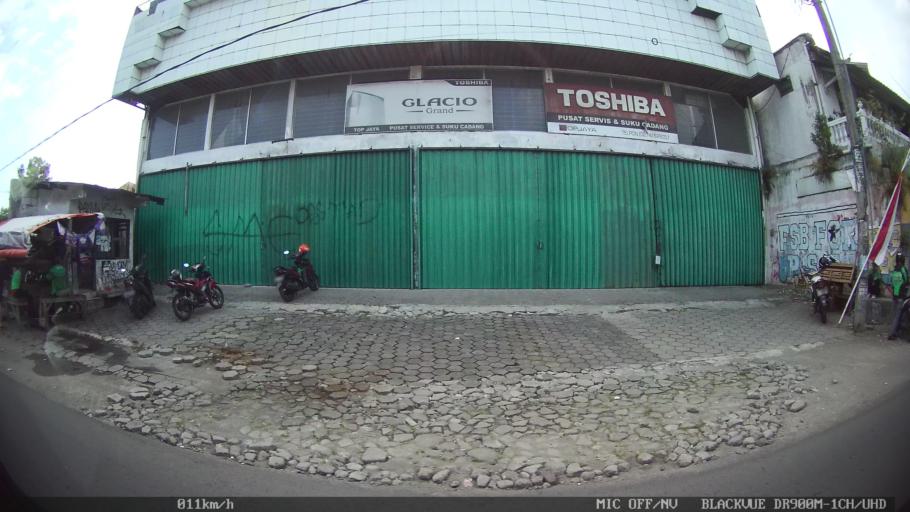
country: ID
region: Daerah Istimewa Yogyakarta
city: Yogyakarta
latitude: -7.7813
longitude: 110.3502
